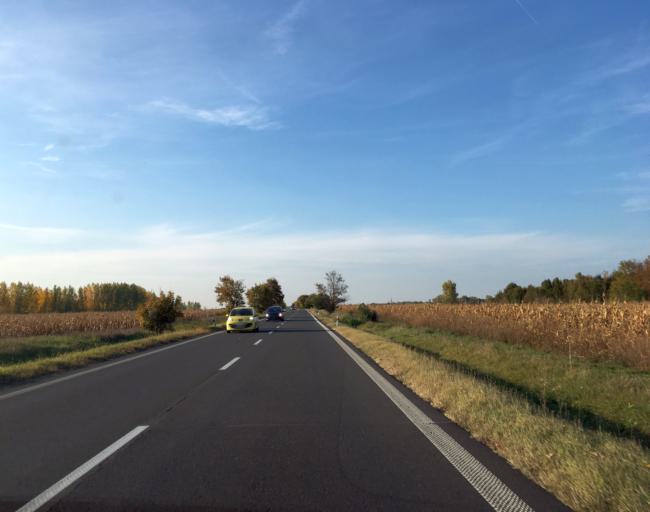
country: SK
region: Nitriansky
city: Surany
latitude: 48.0752
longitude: 18.0855
